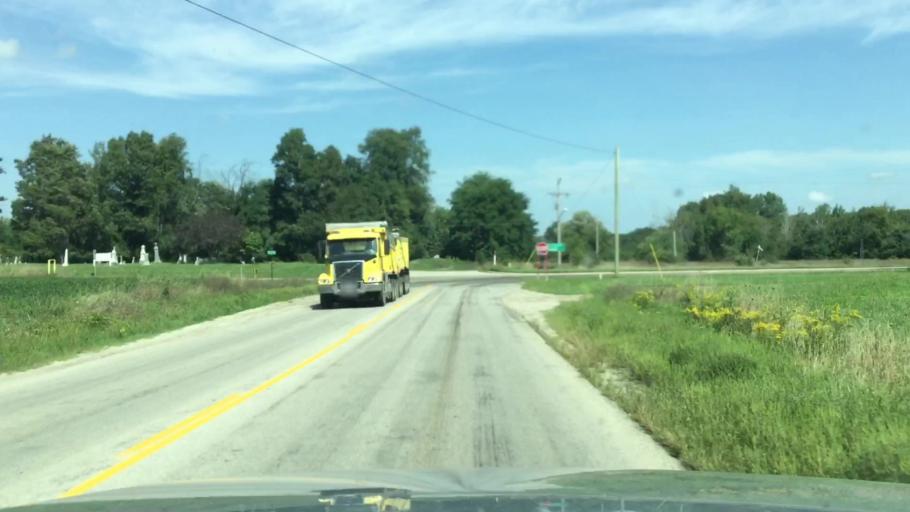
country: US
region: Michigan
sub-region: Jackson County
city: Brooklyn
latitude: 42.0478
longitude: -84.2765
